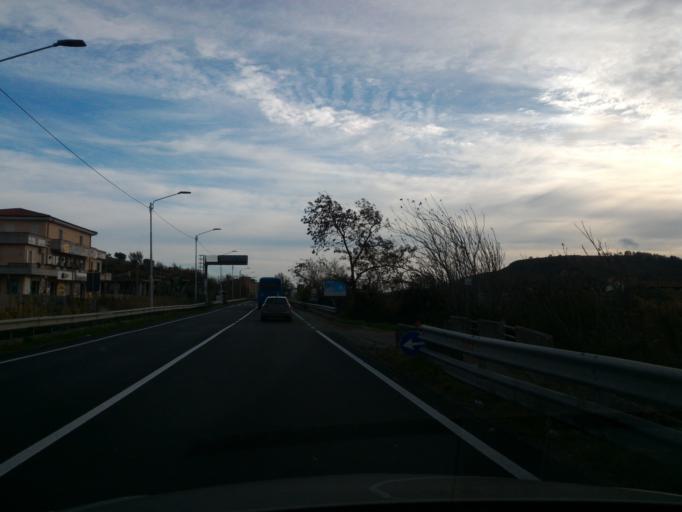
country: IT
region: Calabria
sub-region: Provincia di Catanzaro
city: Catanzaro
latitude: 38.8759
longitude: 16.6041
